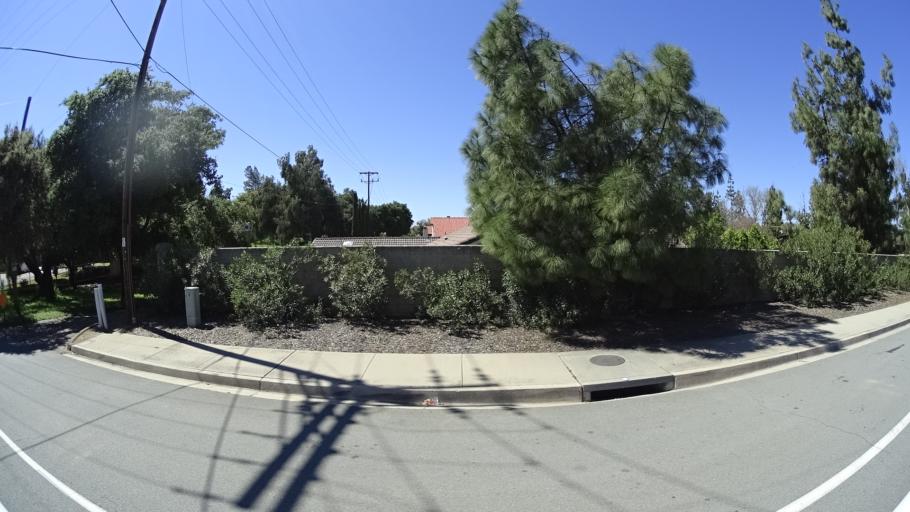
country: US
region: California
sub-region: San Diego County
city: Alpine
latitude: 32.8333
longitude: -116.7753
